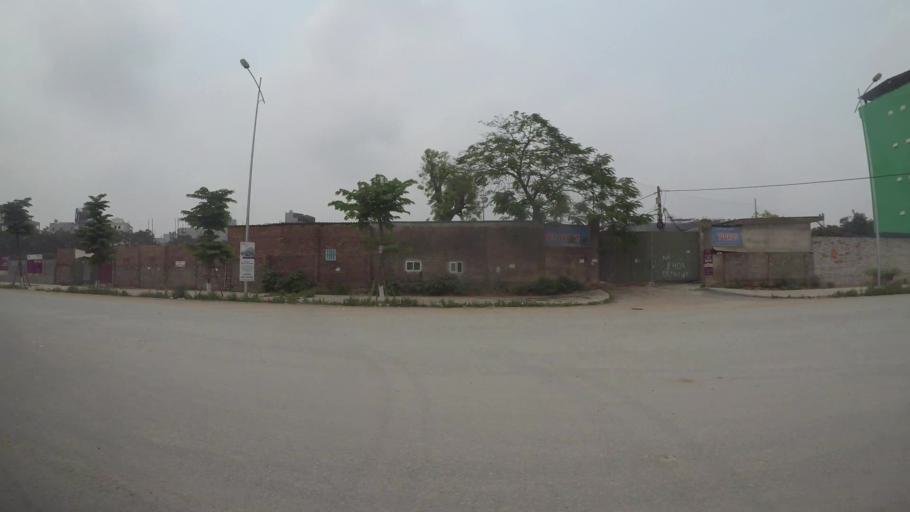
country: VN
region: Ha Noi
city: Ha Dong
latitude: 20.9879
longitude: 105.7535
